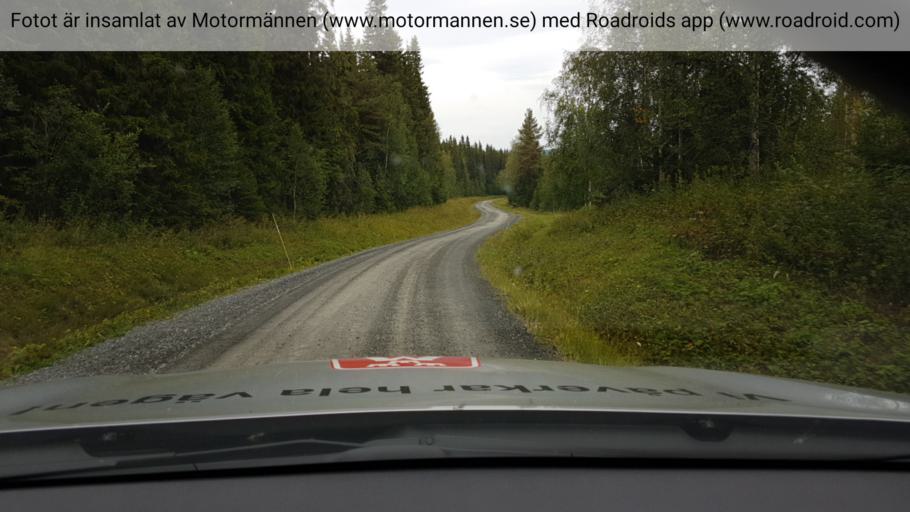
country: SE
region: Jaemtland
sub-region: Krokoms Kommun
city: Valla
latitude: 63.5274
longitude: 13.8998
